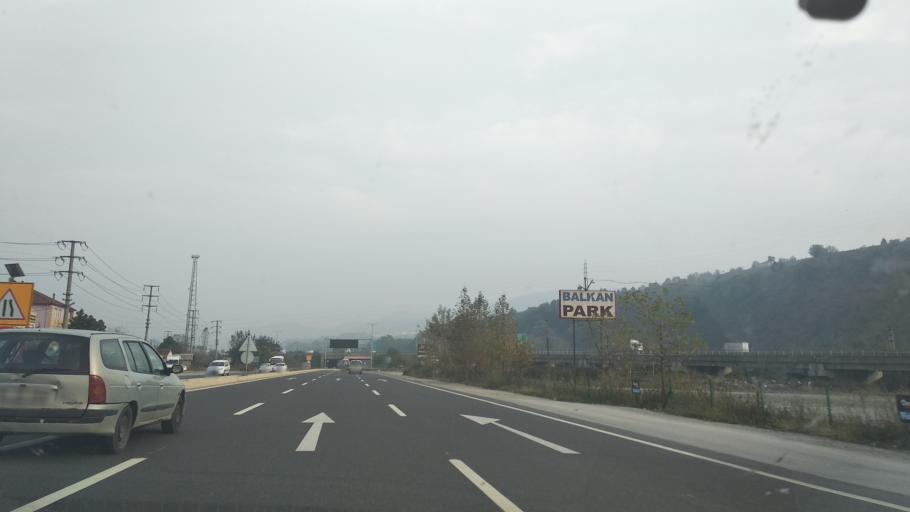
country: TR
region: Duzce
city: Kaynasli
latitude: 40.7875
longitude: 31.2624
